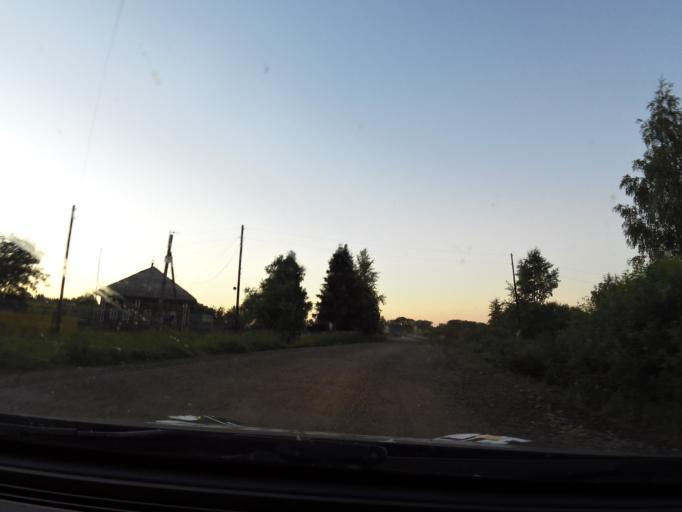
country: RU
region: Kostroma
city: Buy
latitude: 58.4030
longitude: 41.2395
